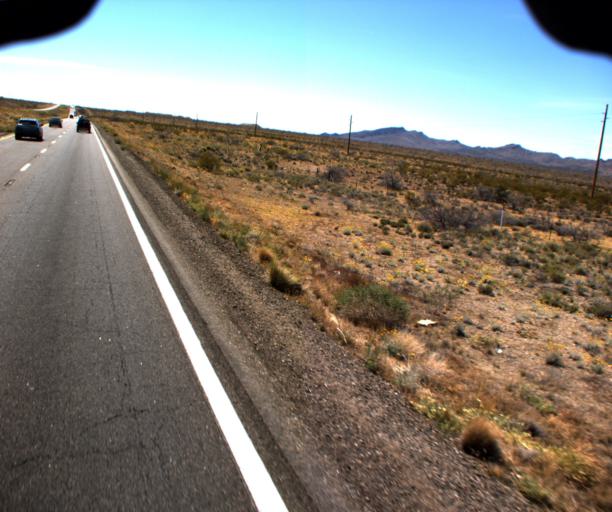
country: US
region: Arizona
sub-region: Mohave County
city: Dolan Springs
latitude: 35.4386
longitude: -114.2897
